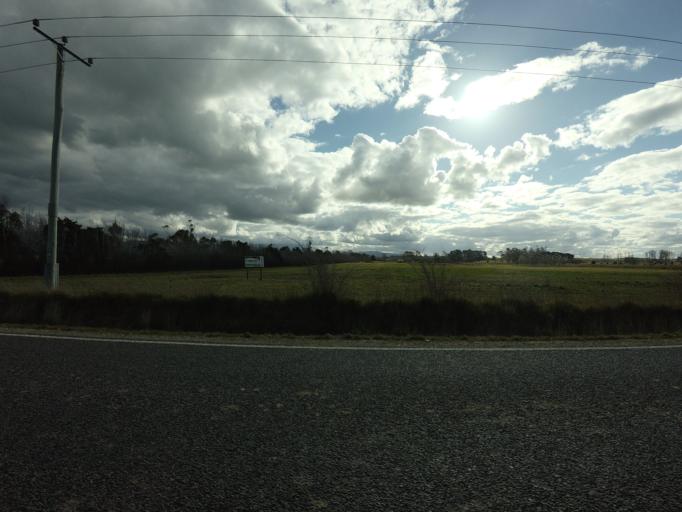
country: AU
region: Tasmania
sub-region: Northern Midlands
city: Longford
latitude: -41.7237
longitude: 147.0894
